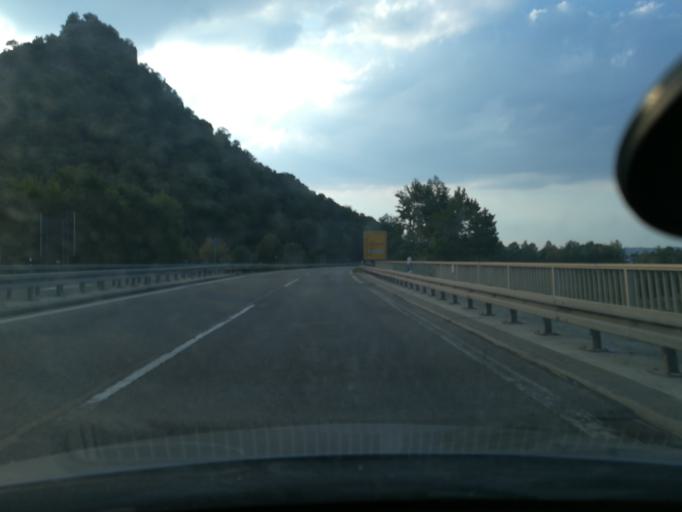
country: DE
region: Baden-Wuerttemberg
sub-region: Freiburg Region
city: Muhlhausen-Ehingen
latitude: 47.7970
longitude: 8.8260
